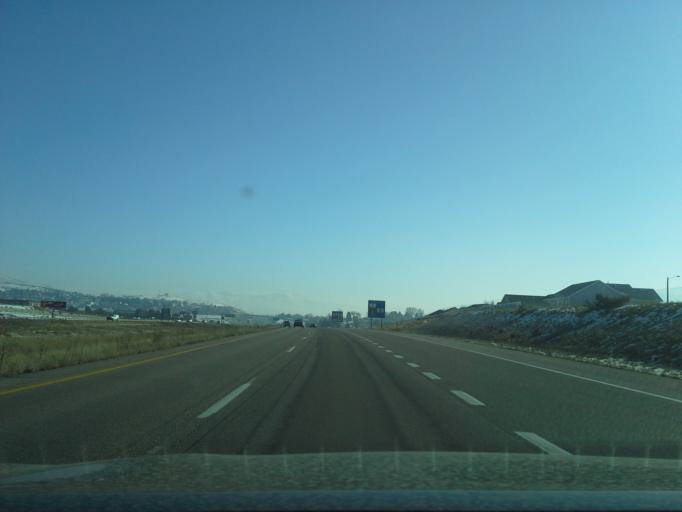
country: US
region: Idaho
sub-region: Bannock County
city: Chubbuck
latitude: 42.9093
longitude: -112.4405
